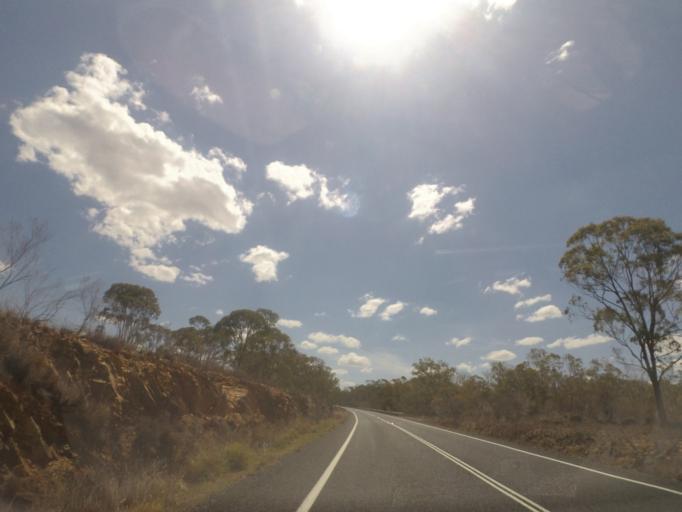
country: AU
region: Queensland
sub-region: Southern Downs
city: Warwick
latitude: -28.1611
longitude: 151.6930
